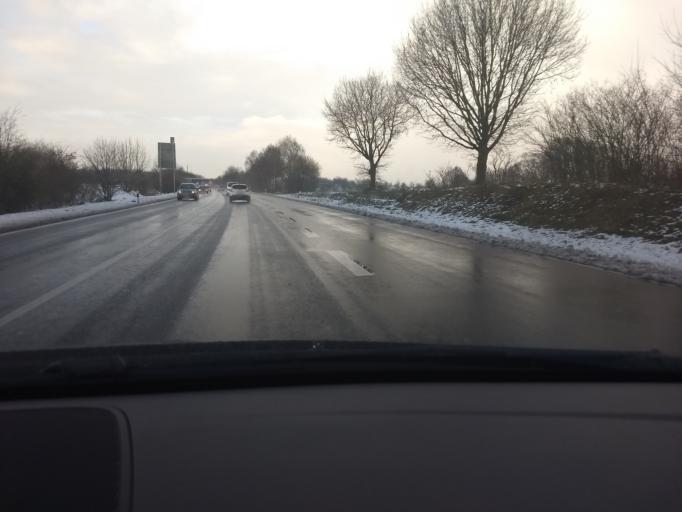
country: DE
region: Lower Saxony
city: Nordhorn
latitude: 52.4320
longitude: 7.0858
